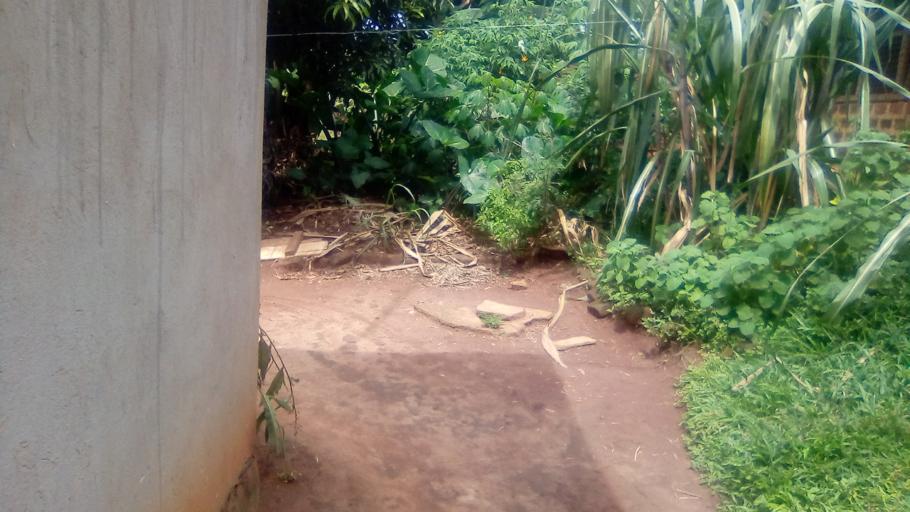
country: UG
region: Central Region
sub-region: Wakiso District
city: Entebbe
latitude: 0.0982
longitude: 32.5297
